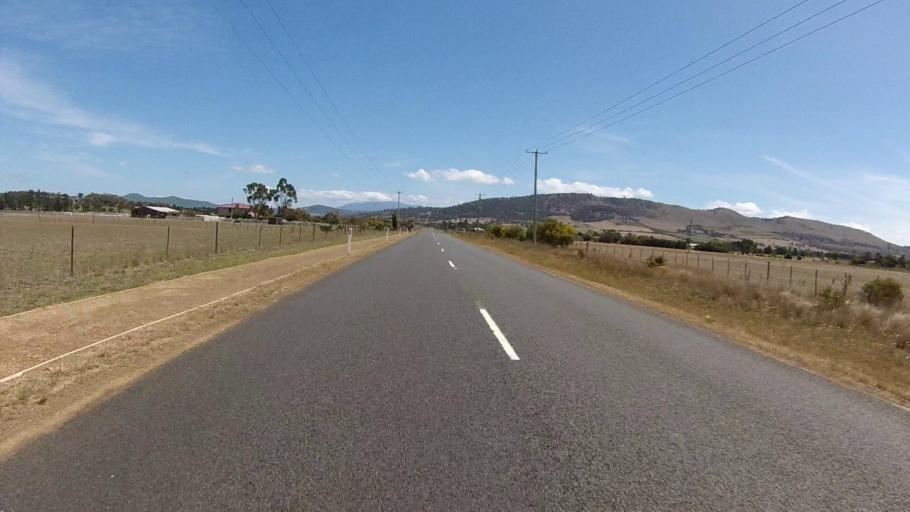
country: AU
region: Tasmania
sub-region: Sorell
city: Sorell
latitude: -42.7757
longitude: 147.5328
